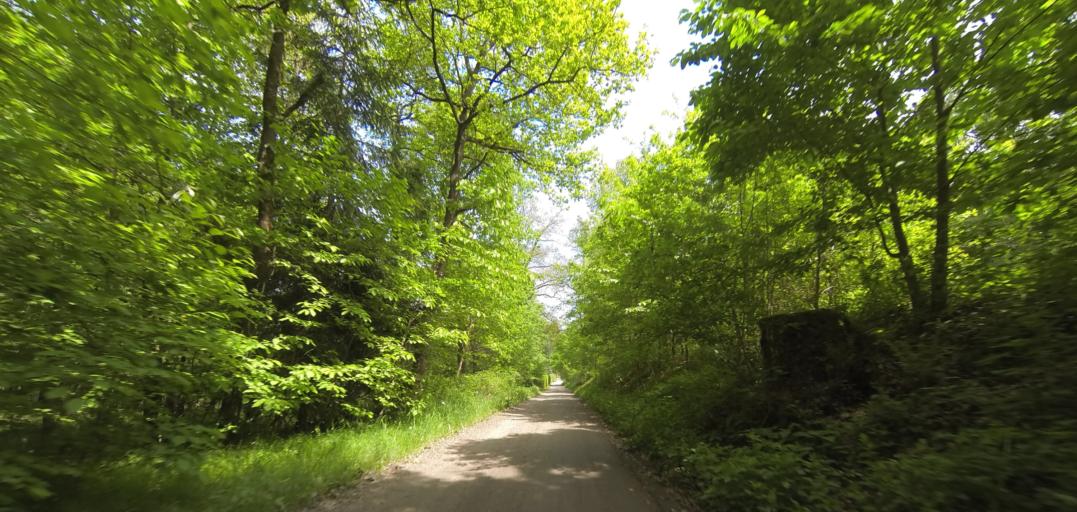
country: DE
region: Saxony
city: Grossharthau
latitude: 51.1006
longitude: 14.0778
